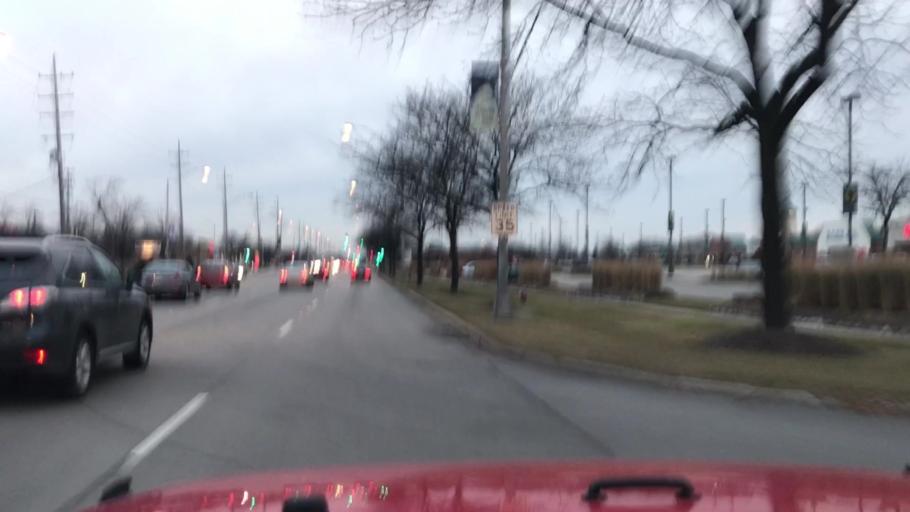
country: US
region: Illinois
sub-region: Cook County
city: Arlington Heights
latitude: 42.1108
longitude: -87.9774
